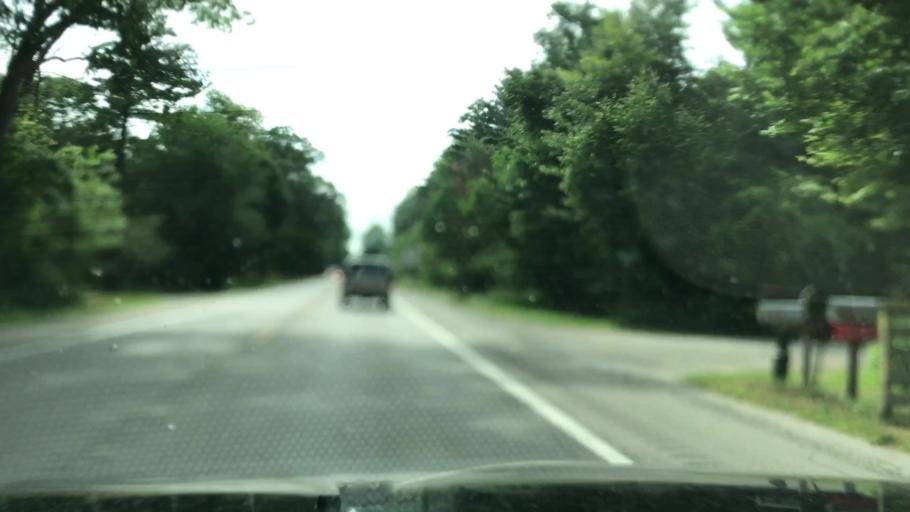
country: US
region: Michigan
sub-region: Muskegon County
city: Fruitport
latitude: 43.0740
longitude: -86.1294
